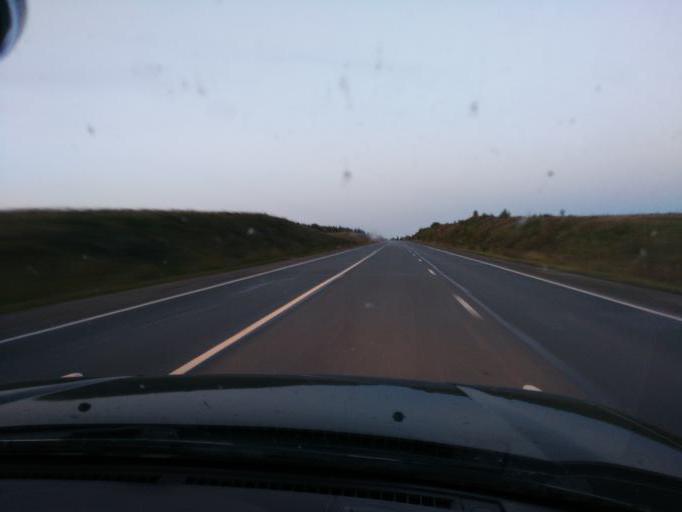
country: RU
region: Perm
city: Verkhnechusovskiye Gorodki
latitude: 58.2242
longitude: 57.1888
